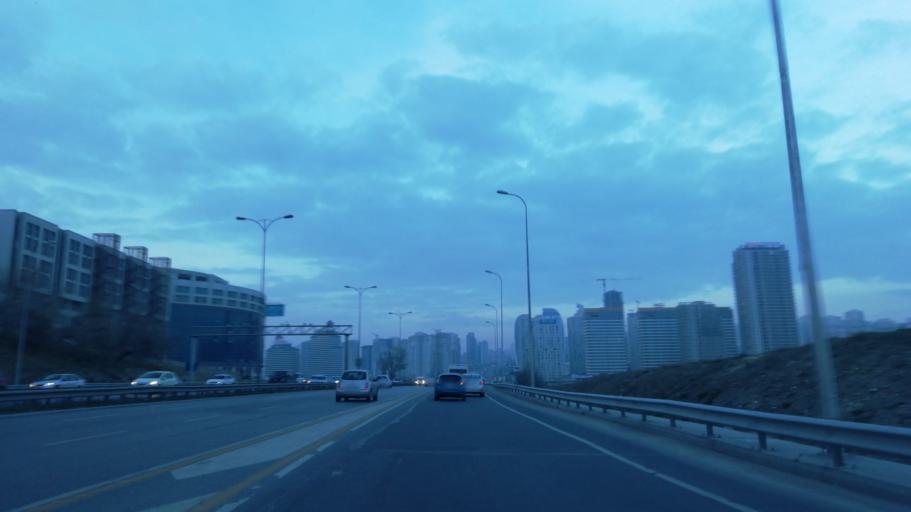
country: TR
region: Istanbul
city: Yakuplu
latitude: 41.0014
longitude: 28.6774
